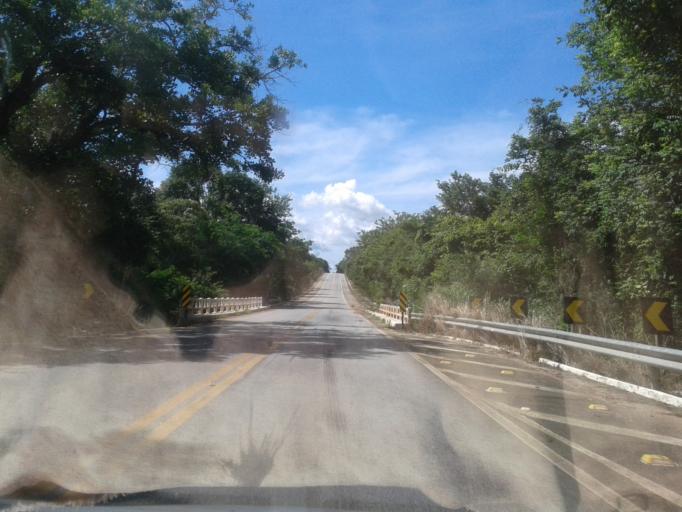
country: BR
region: Goias
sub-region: Goias
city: Goias
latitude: -15.7046
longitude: -50.1947
